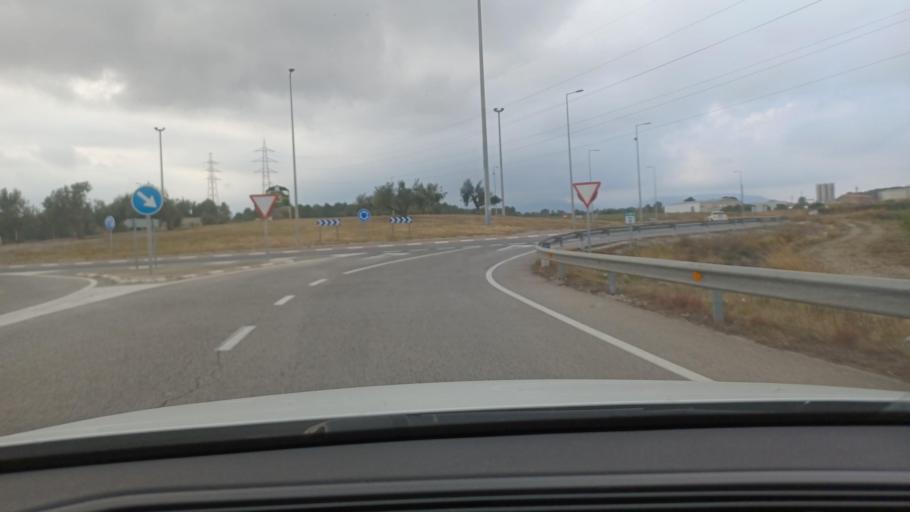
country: ES
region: Catalonia
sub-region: Provincia de Tarragona
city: la Pobla de Mafumet
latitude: 41.2014
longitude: 1.2442
